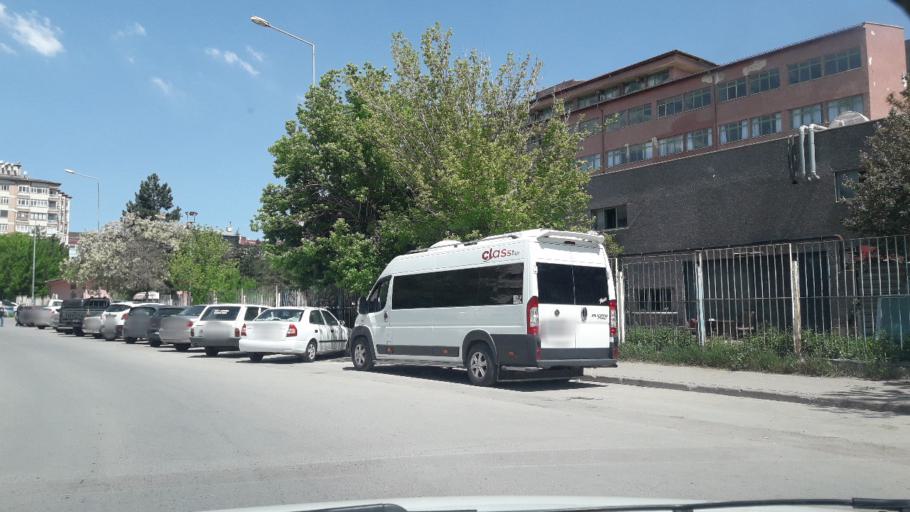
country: TR
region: Sivas
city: Sivas
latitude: 39.7436
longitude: 37.0119
